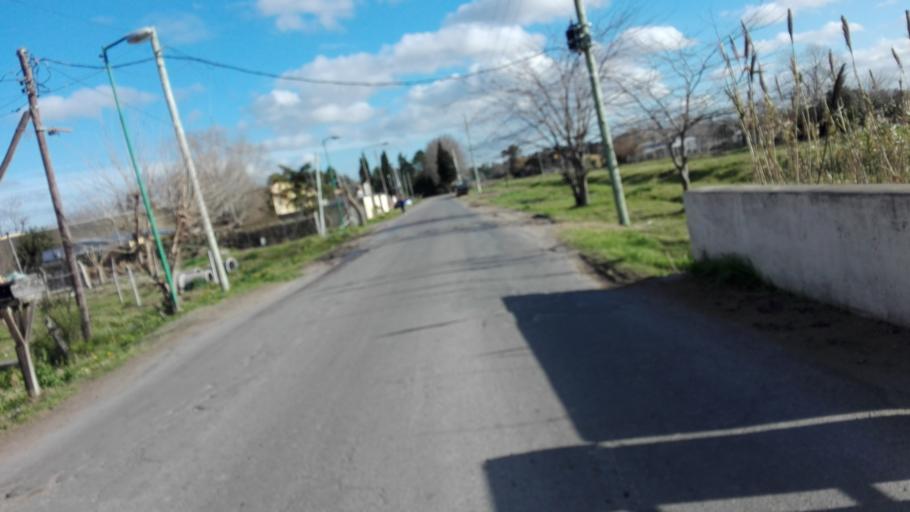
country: AR
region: Buenos Aires
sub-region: Partido de La Plata
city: La Plata
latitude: -34.9128
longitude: -58.0231
